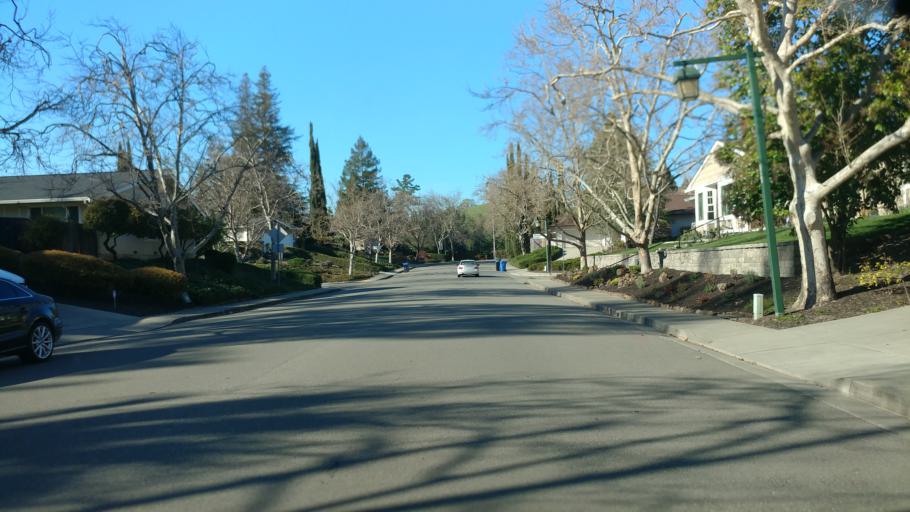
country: US
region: California
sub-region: Contra Costa County
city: Danville
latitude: 37.8182
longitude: -121.9761
